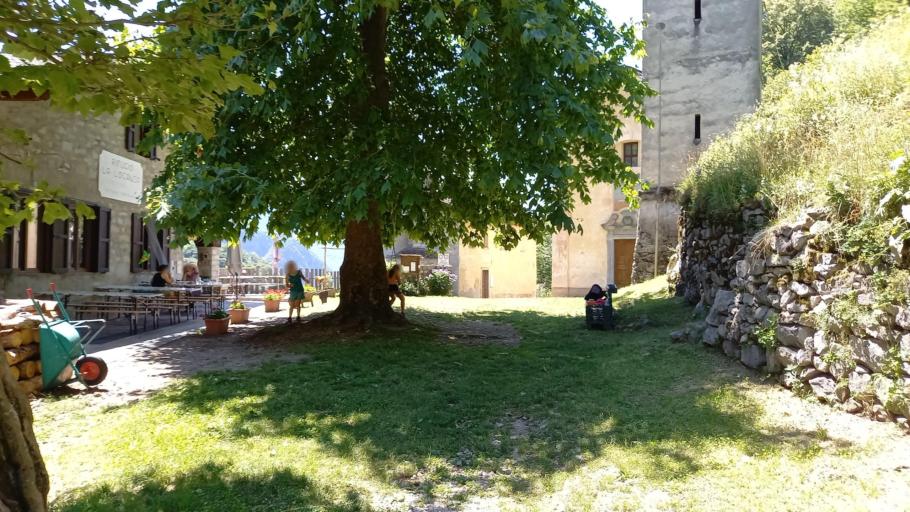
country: IT
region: Lombardy
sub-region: Provincia di Sondrio
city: Novate Mezzola
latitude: 46.2384
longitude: 9.4729
